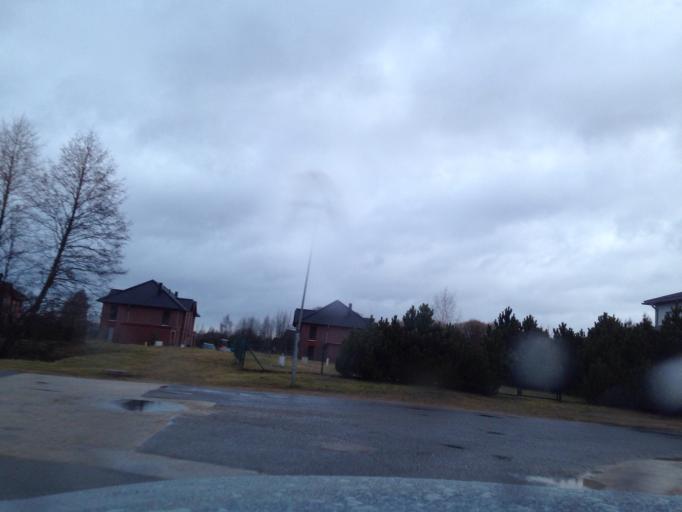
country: LV
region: Marupe
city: Marupe
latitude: 56.8889
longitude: 24.0345
